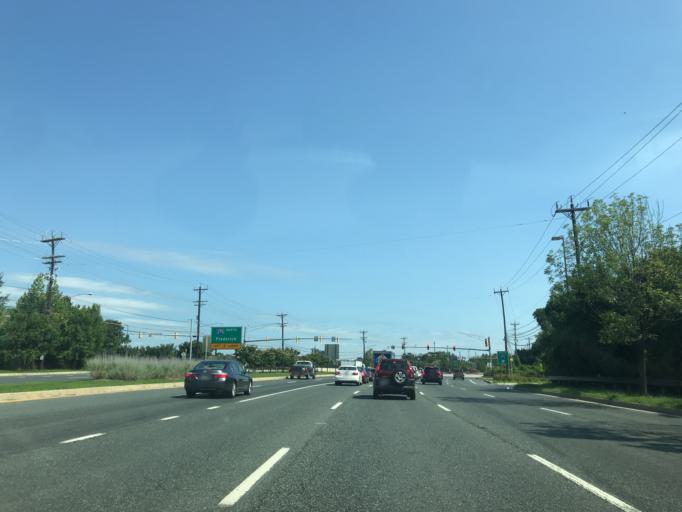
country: US
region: Maryland
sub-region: Montgomery County
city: North Bethesda
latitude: 39.0290
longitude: -77.1264
